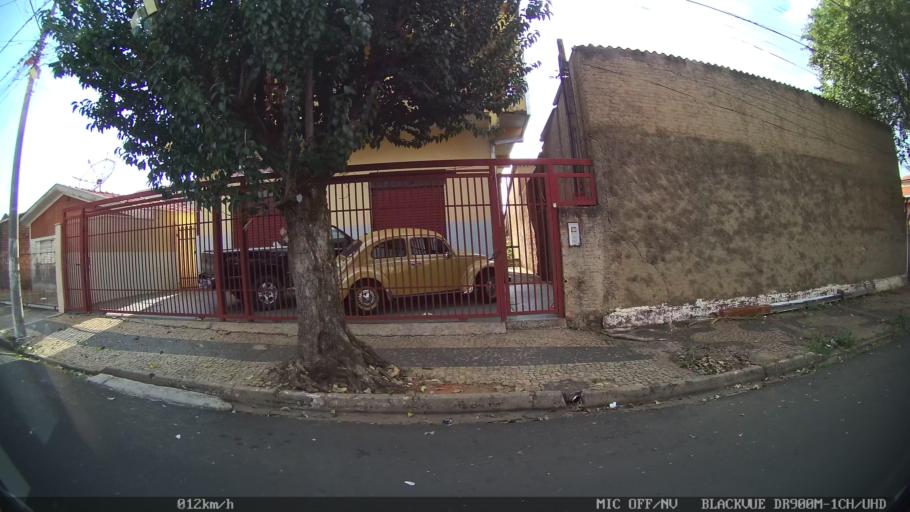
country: BR
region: Sao Paulo
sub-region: Americana
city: Americana
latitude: -22.7254
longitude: -47.3680
